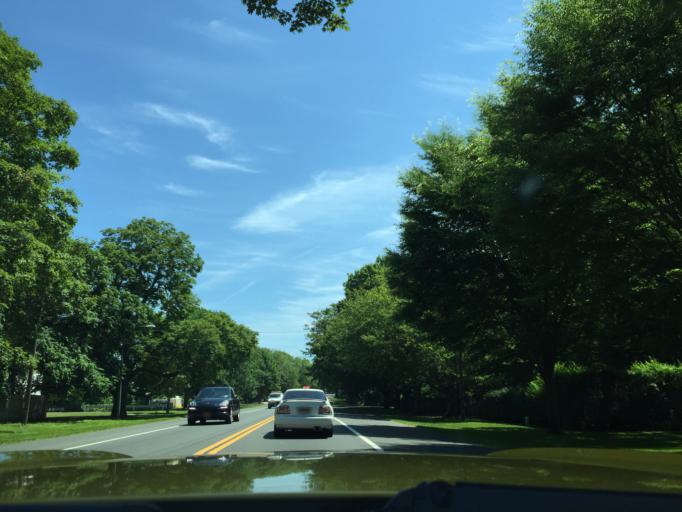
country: US
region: New York
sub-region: Suffolk County
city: East Hampton
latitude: 40.9671
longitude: -72.1756
